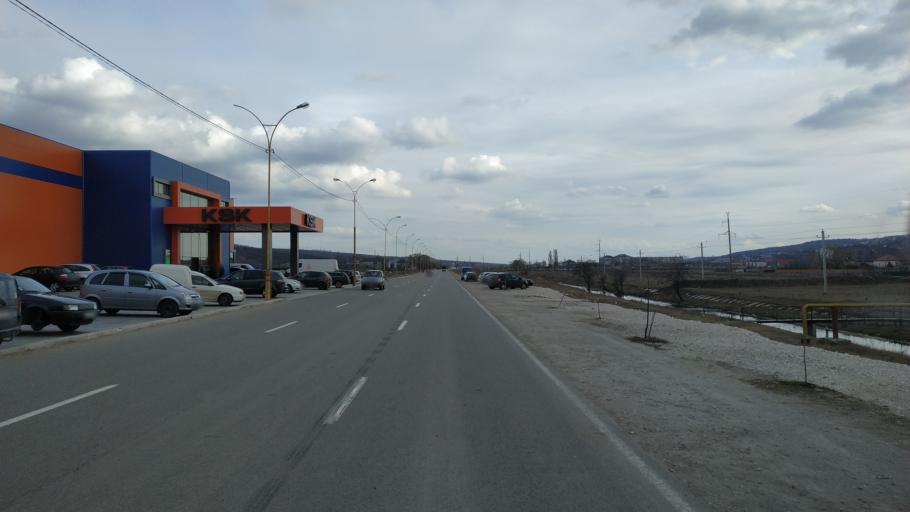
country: MD
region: Hincesti
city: Hincesti
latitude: 46.8302
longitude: 28.5996
